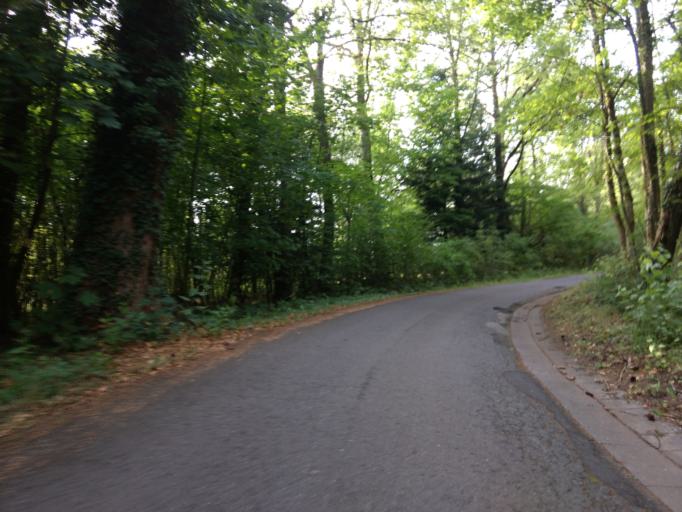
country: DE
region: Saarland
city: Rehlingen-Siersburg
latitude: 49.3424
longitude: 6.6848
